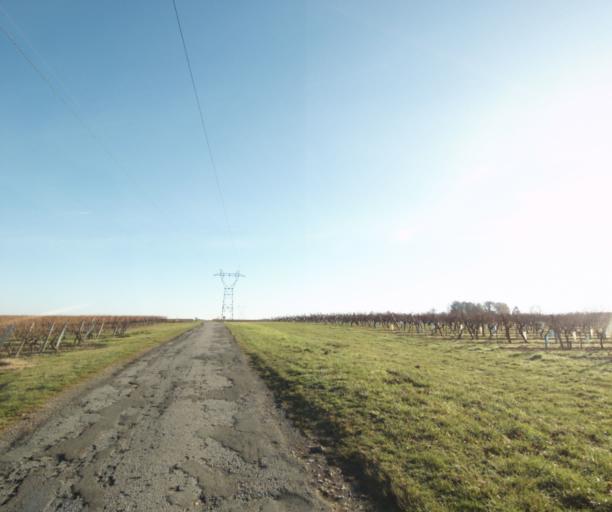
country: FR
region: Poitou-Charentes
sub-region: Departement de la Charente-Maritime
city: Cherac
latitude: 45.7399
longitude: -0.4511
